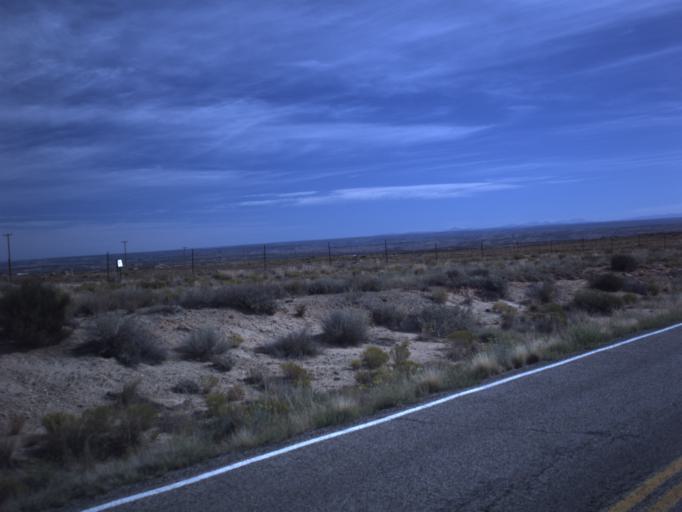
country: US
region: Utah
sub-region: San Juan County
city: Blanding
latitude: 37.3254
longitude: -109.3336
